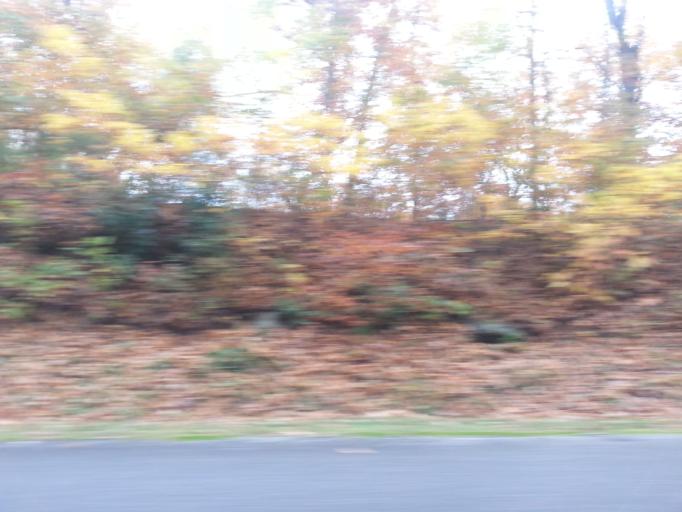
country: US
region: North Carolina
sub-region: Ashe County
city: Jefferson
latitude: 36.2965
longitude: -81.3664
